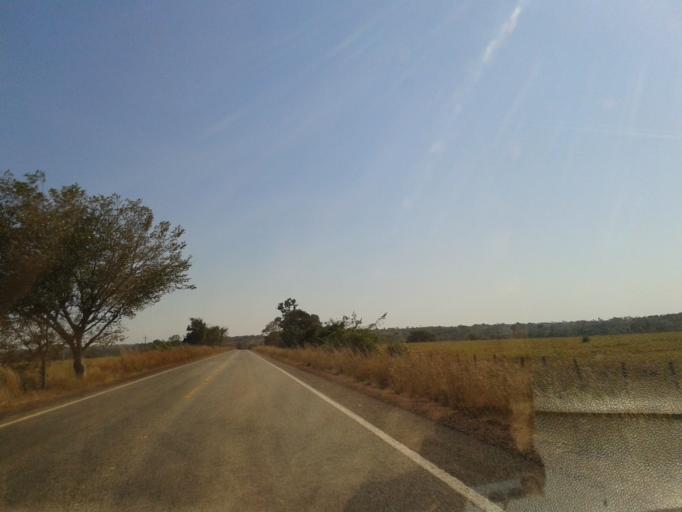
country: BR
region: Goias
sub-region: Mozarlandia
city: Mozarlandia
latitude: -14.5002
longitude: -50.4846
